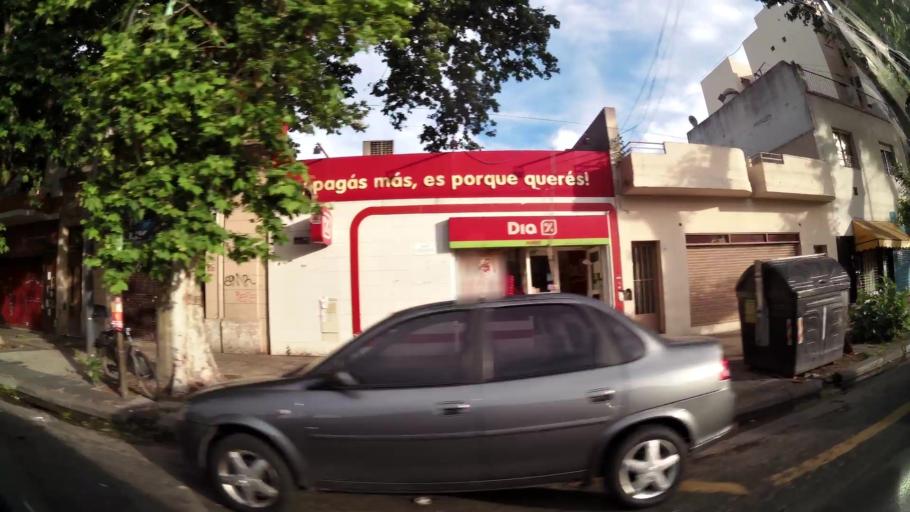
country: AR
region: Buenos Aires F.D.
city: Buenos Aires
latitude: -34.6446
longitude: -58.4249
